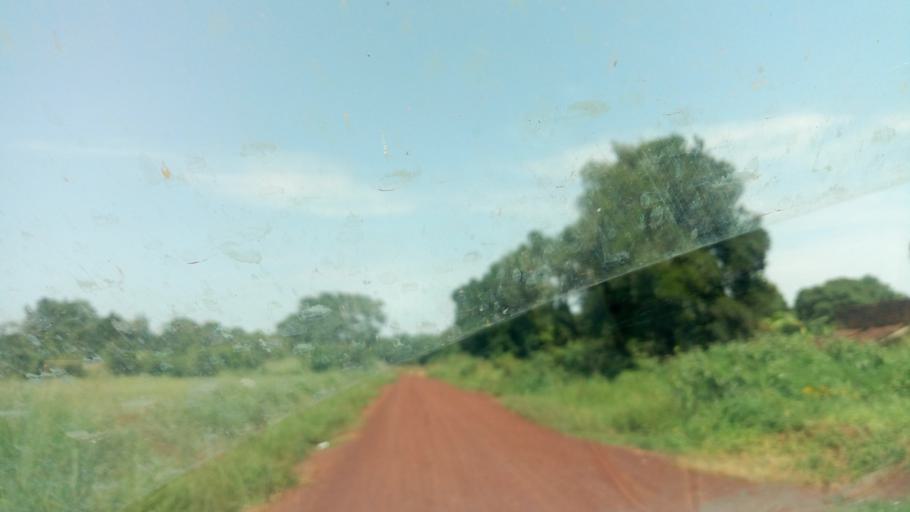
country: UG
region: Western Region
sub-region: Masindi District
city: Masindi
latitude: 1.6688
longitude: 31.8216
